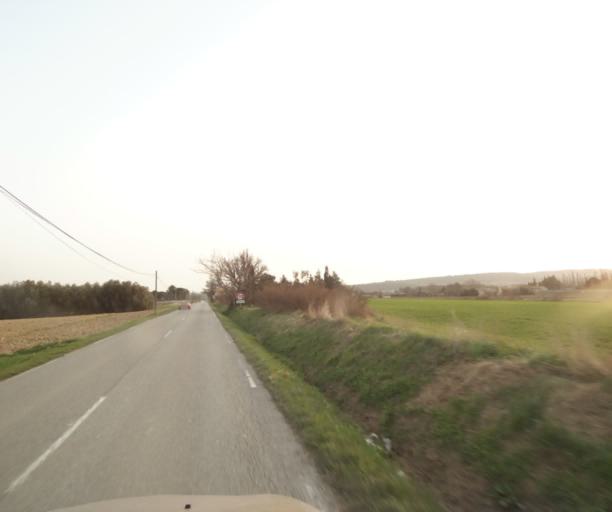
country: FR
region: Provence-Alpes-Cote d'Azur
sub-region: Departement des Bouches-du-Rhone
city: Eguilles
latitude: 43.5537
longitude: 5.3501
